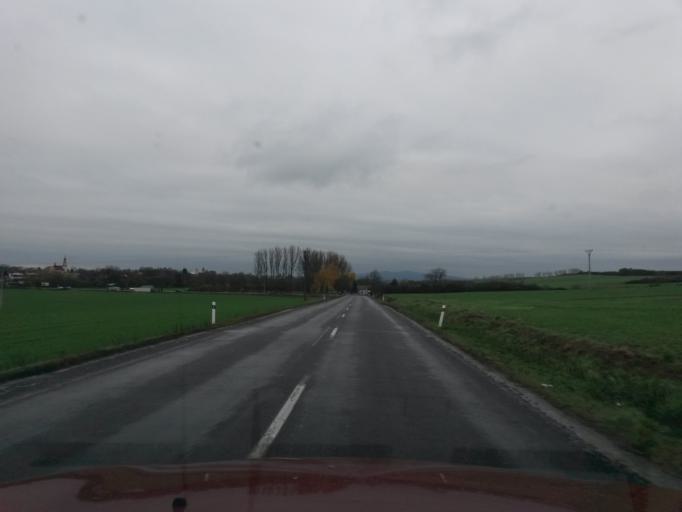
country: SK
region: Kosicky
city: Secovce
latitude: 48.6095
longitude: 21.6172
